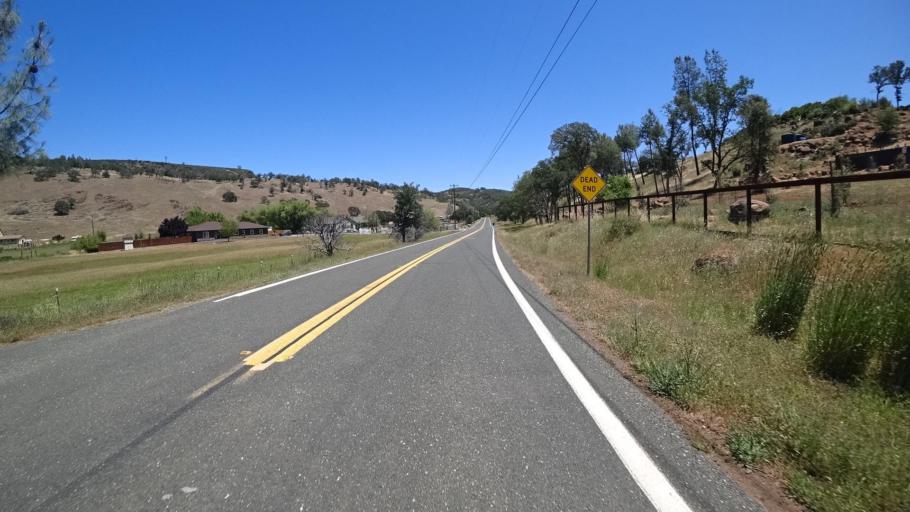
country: US
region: California
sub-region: Lake County
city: Hidden Valley Lake
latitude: 38.8001
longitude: -122.5416
